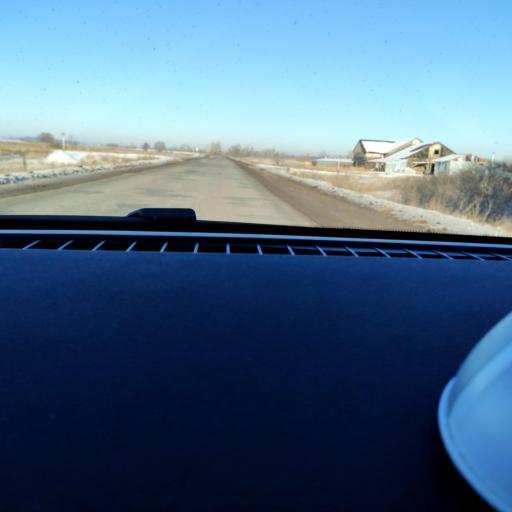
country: RU
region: Samara
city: Spiridonovka
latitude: 53.1158
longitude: 50.6356
